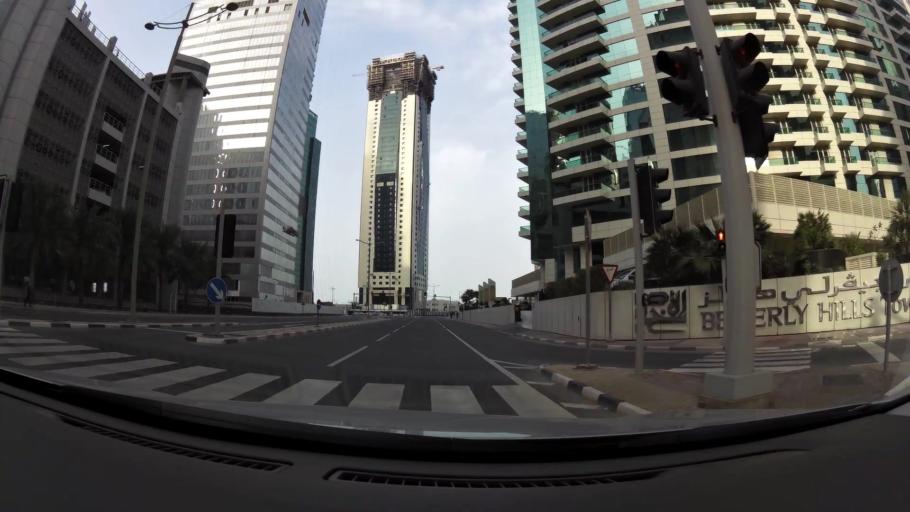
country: QA
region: Baladiyat ad Dawhah
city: Doha
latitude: 25.3261
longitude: 51.5347
